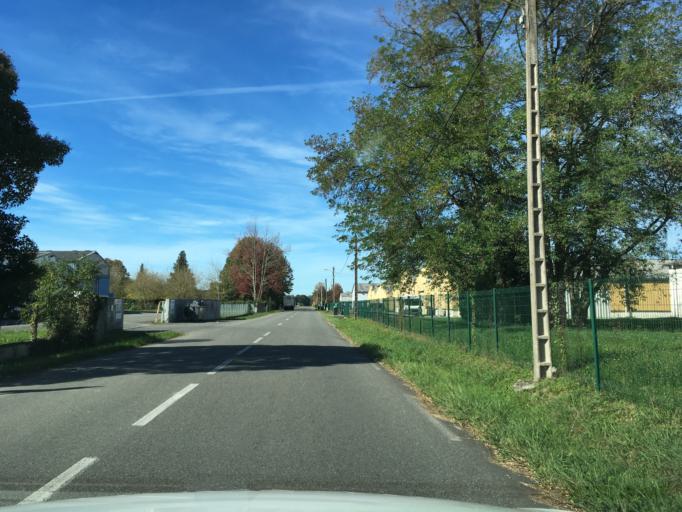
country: FR
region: Aquitaine
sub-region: Departement des Pyrenees-Atlantiques
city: Buros
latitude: 43.3249
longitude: -0.2997
